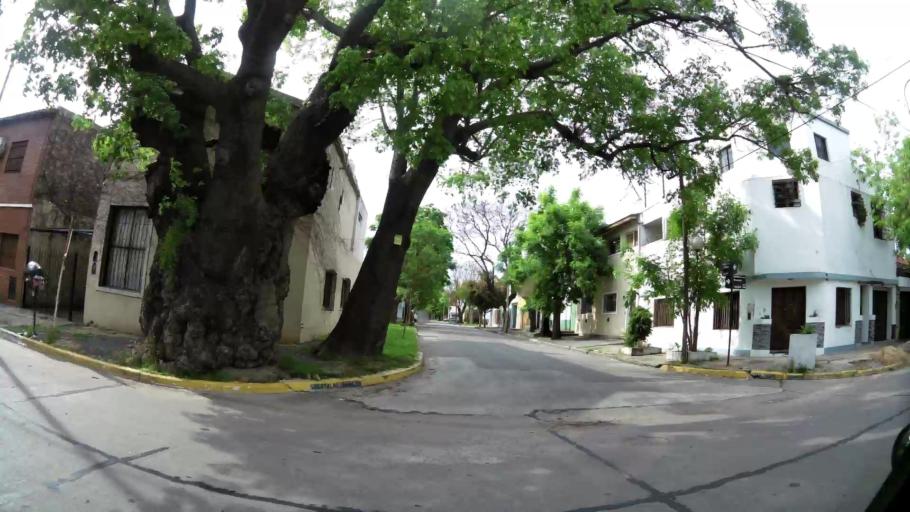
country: AR
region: Buenos Aires
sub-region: Partido de Quilmes
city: Quilmes
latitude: -34.7219
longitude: -58.2445
